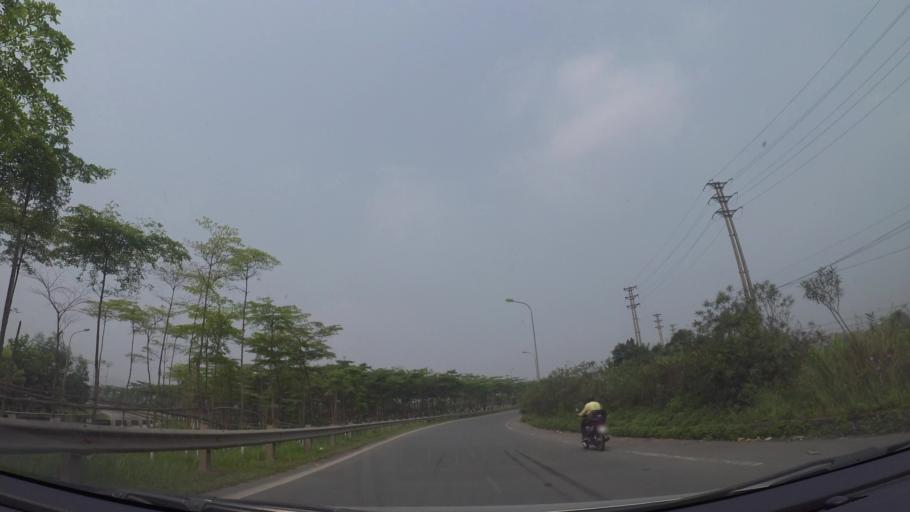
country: VN
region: Ha Noi
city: Lien Quan
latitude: 20.9930
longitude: 105.5253
